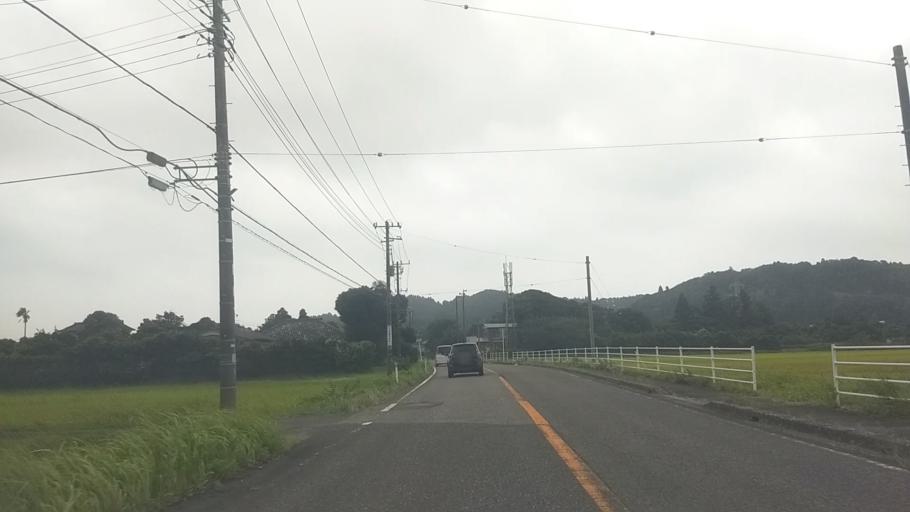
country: JP
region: Chiba
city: Ohara
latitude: 35.2618
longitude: 140.3754
